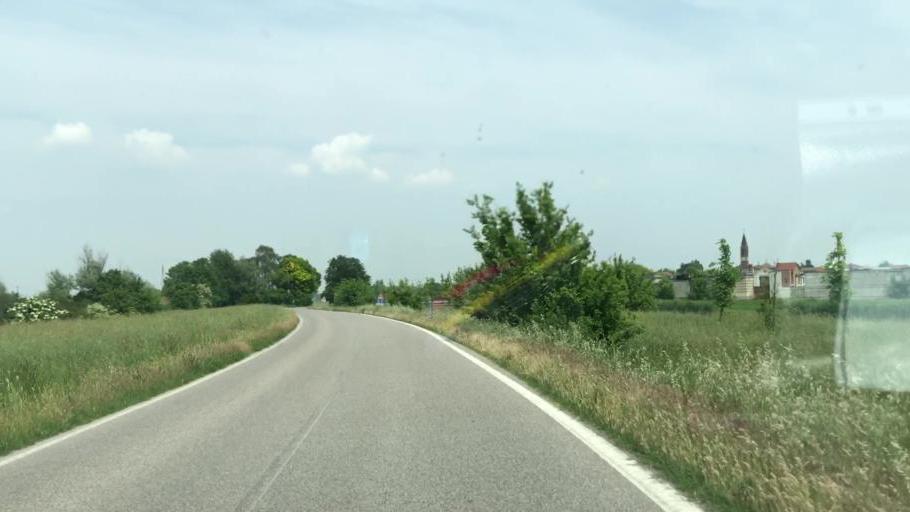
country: IT
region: Lombardy
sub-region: Provincia di Mantova
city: Dosolo
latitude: 45.0156
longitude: 10.6186
